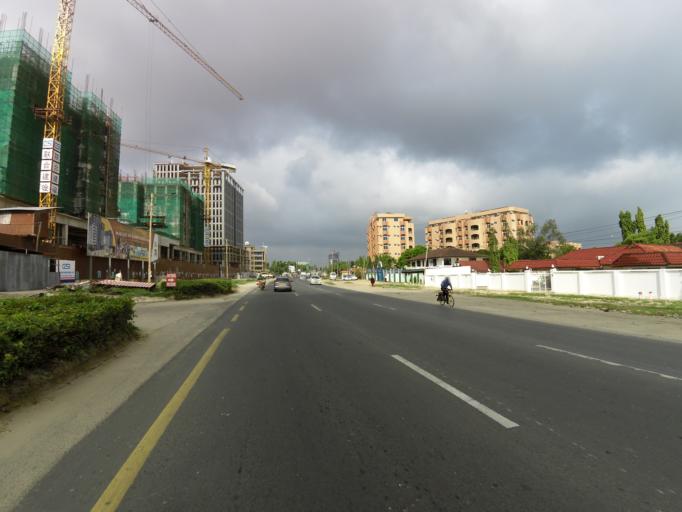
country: TZ
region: Dar es Salaam
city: Magomeni
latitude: -6.7786
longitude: 39.2543
